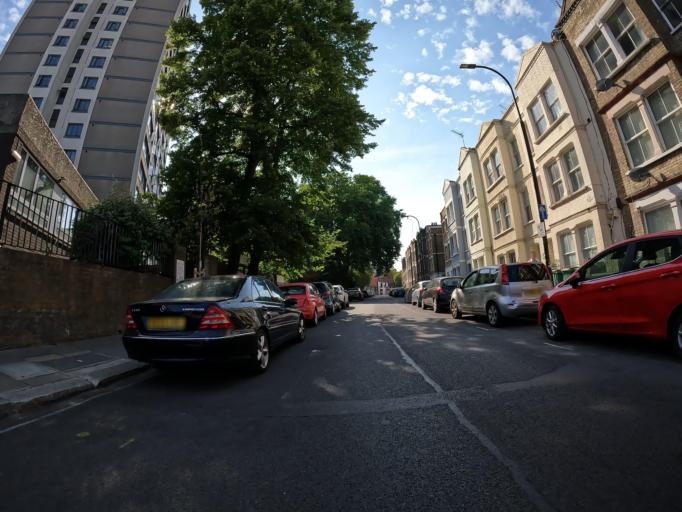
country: GB
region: England
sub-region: Greater London
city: Hendon
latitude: 51.5902
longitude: -0.2221
